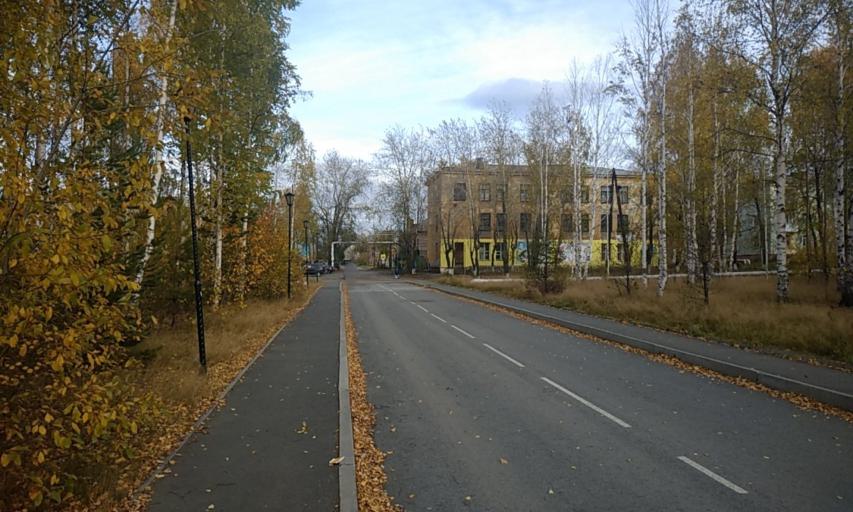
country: RU
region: Sverdlovsk
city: Krasnoural'sk
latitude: 58.3555
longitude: 60.0546
